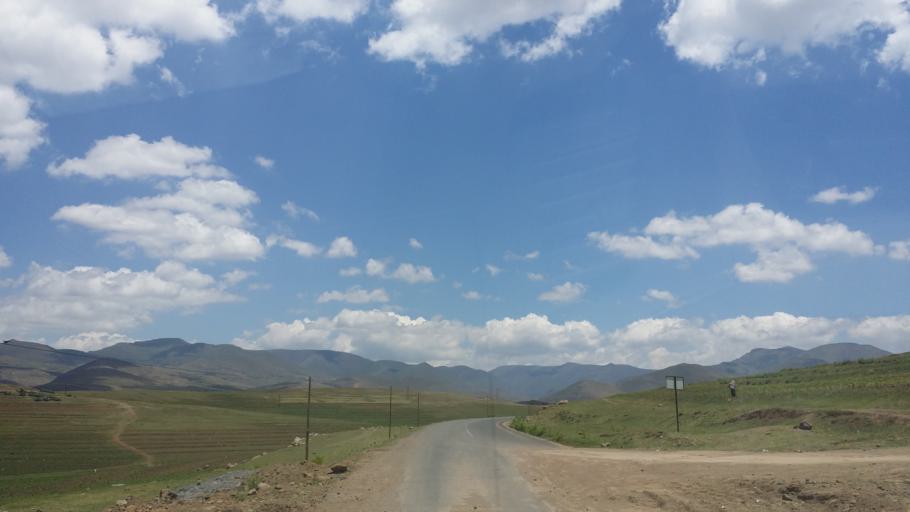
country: LS
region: Mokhotlong
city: Mokhotlong
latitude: -29.2197
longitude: 28.9025
